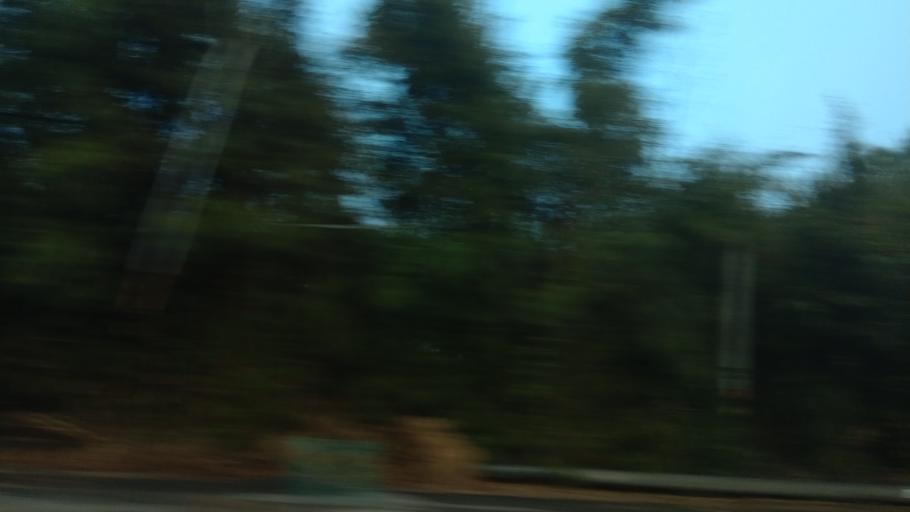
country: TW
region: Taiwan
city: Daxi
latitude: 24.8807
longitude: 121.2201
